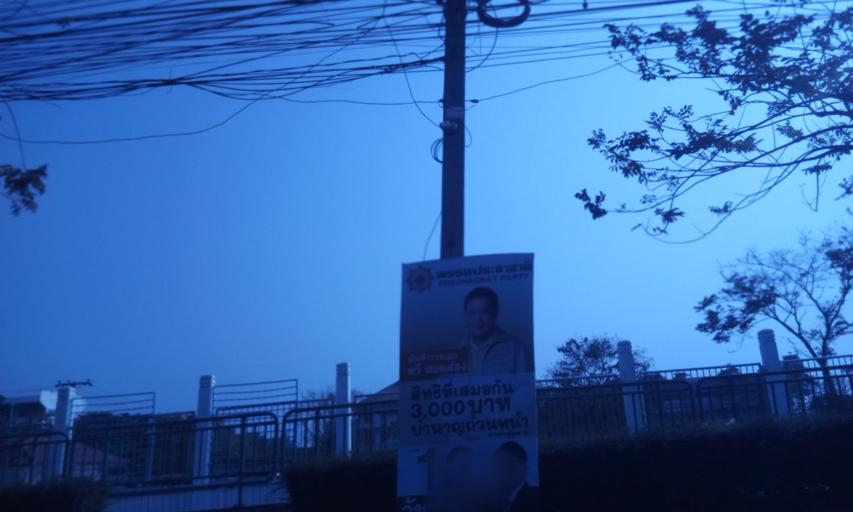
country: TH
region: Bangkok
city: Don Mueang
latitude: 13.9290
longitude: 100.5799
